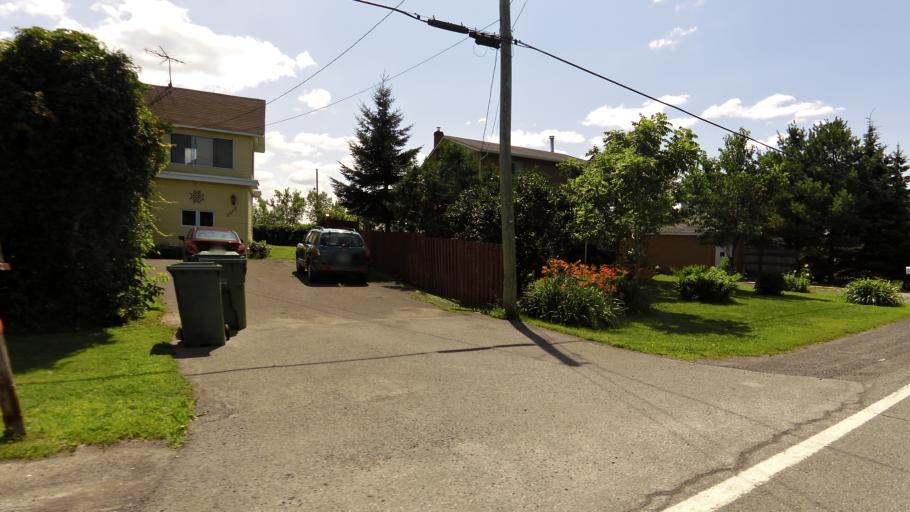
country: CA
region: Quebec
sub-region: Monteregie
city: Richelieu
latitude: 45.4070
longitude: -73.2560
